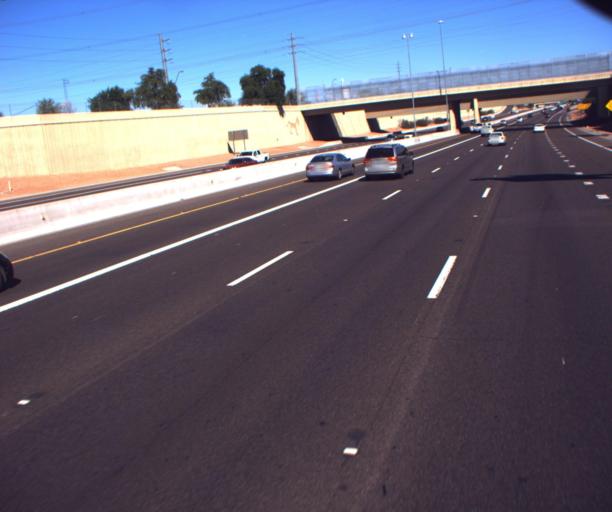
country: US
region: Arizona
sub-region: Maricopa County
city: San Carlos
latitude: 33.3552
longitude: -111.8942
